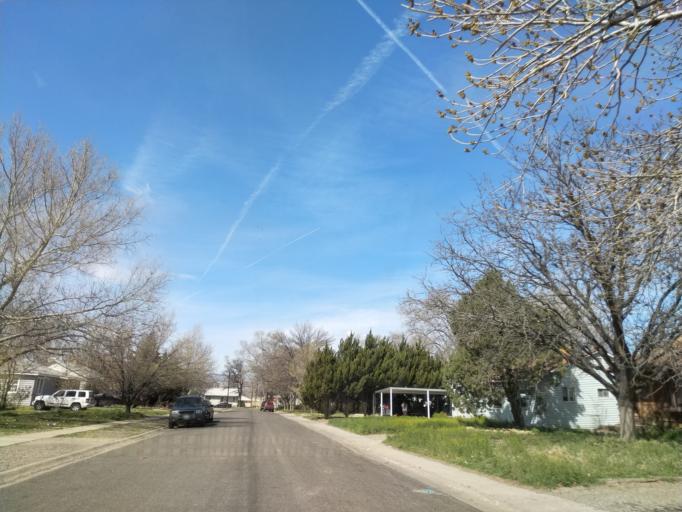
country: US
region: Colorado
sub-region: Mesa County
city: Grand Junction
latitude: 39.0835
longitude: -108.5580
